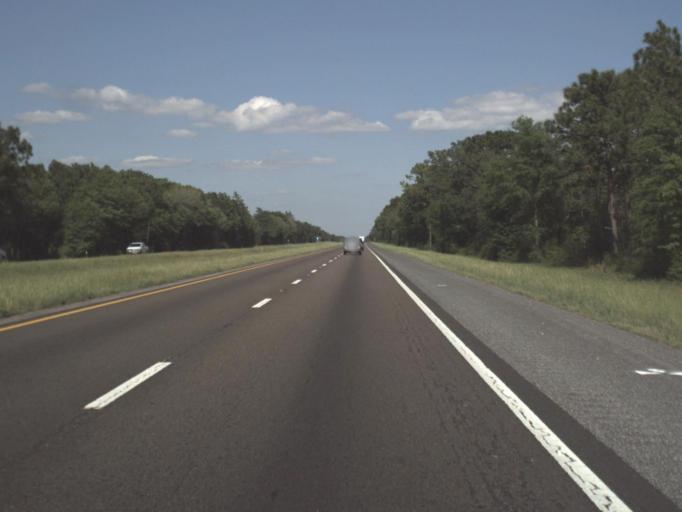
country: US
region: Florida
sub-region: Santa Rosa County
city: East Milton
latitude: 30.6403
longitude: -86.9102
